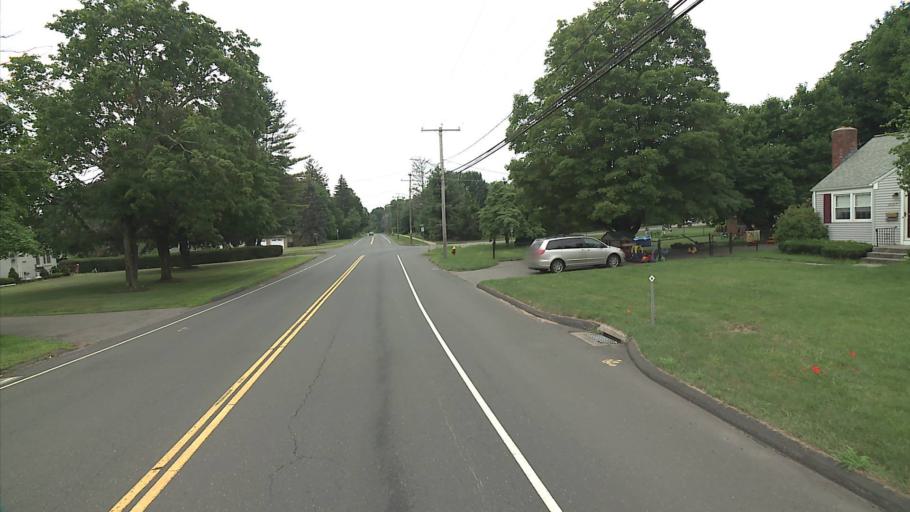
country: US
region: Connecticut
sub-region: Middlesex County
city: Cromwell
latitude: 41.6461
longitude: -72.6453
